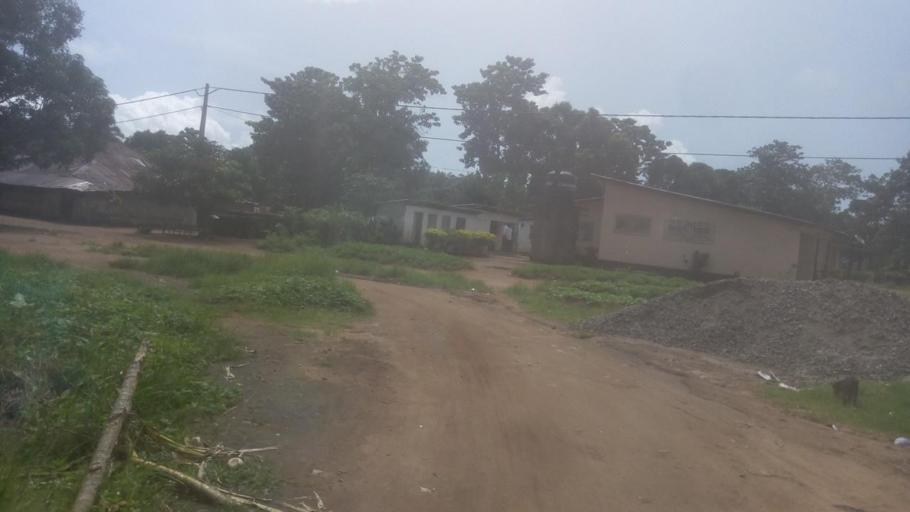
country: SL
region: Northern Province
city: Tintafor
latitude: 8.6340
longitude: -13.2184
